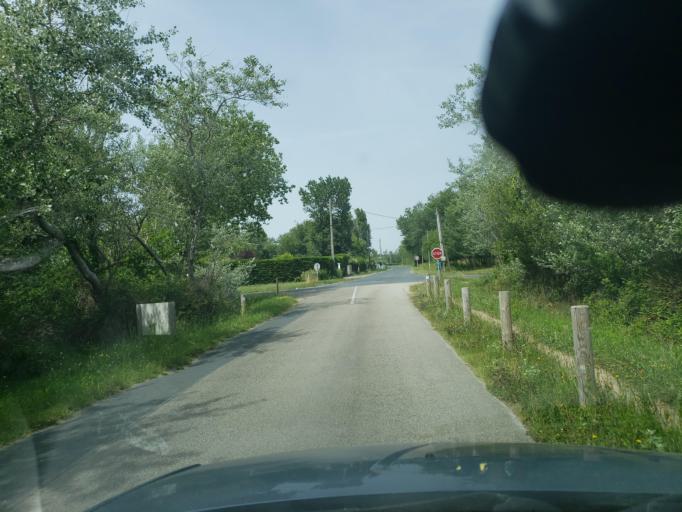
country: FR
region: Brittany
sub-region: Departement du Finistere
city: Guilvinec
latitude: 47.8029
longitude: -4.3192
